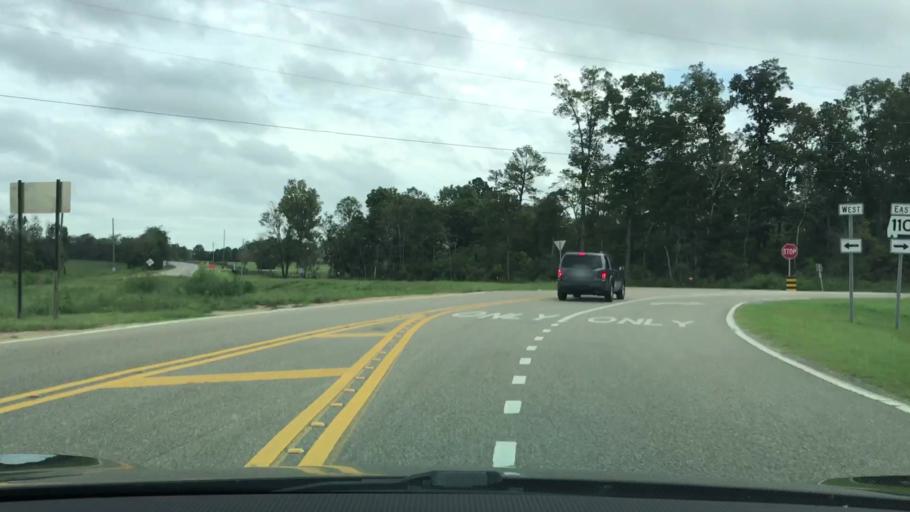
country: US
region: Alabama
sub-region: Montgomery County
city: Pike Road
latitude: 32.3138
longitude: -86.0472
